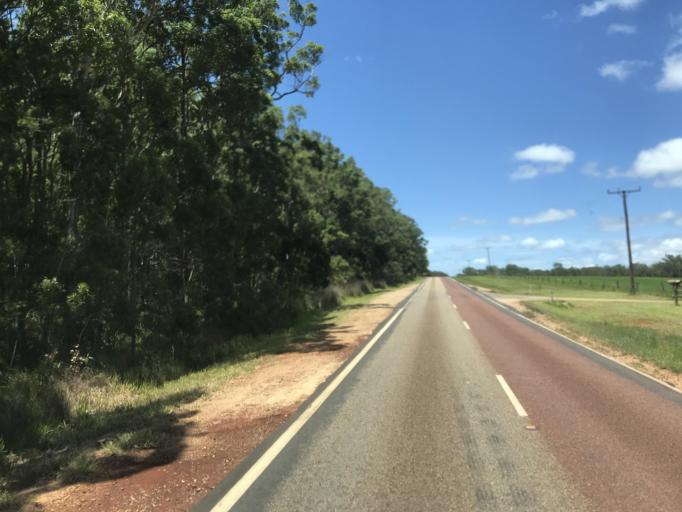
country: AU
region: Queensland
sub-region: Tablelands
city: Ravenshoe
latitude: -17.5236
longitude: 145.4529
